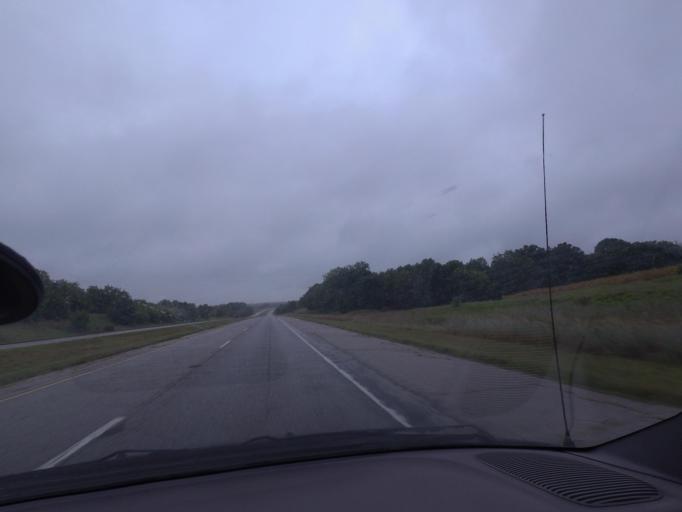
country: US
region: Illinois
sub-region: Pike County
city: Barry
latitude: 39.6928
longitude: -90.9597
